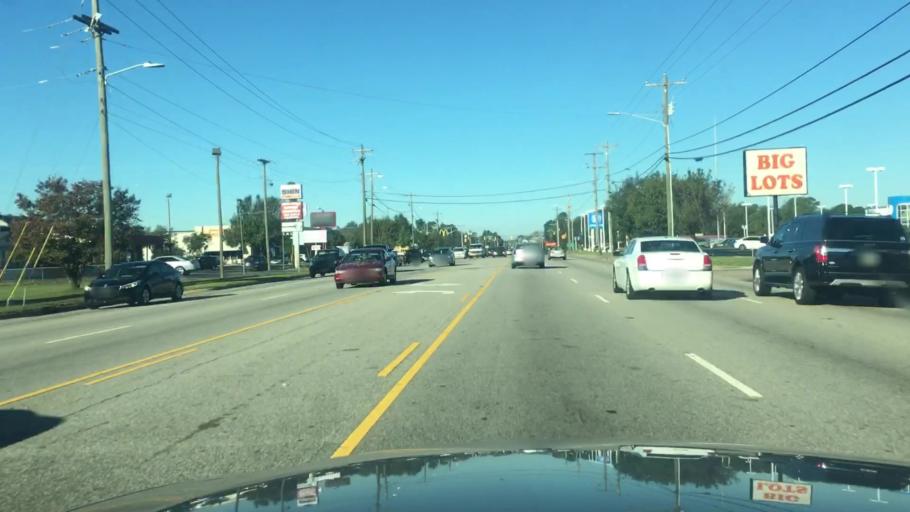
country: US
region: North Carolina
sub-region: Cumberland County
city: Fayetteville
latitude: 35.0439
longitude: -78.9444
